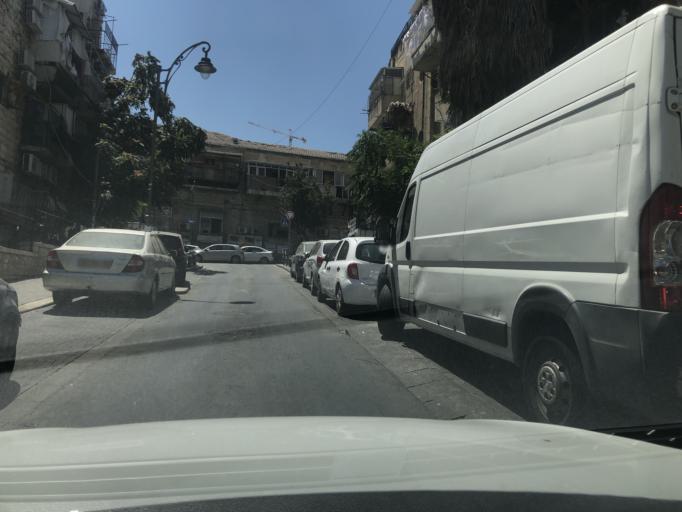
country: IL
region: Jerusalem
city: West Jerusalem
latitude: 31.7885
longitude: 35.2199
